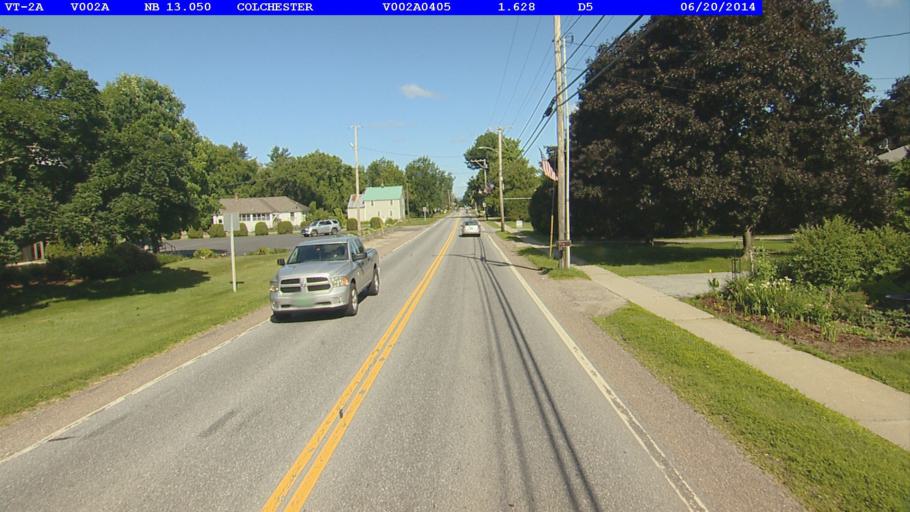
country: US
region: Vermont
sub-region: Chittenden County
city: Colchester
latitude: 44.5449
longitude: -73.1508
